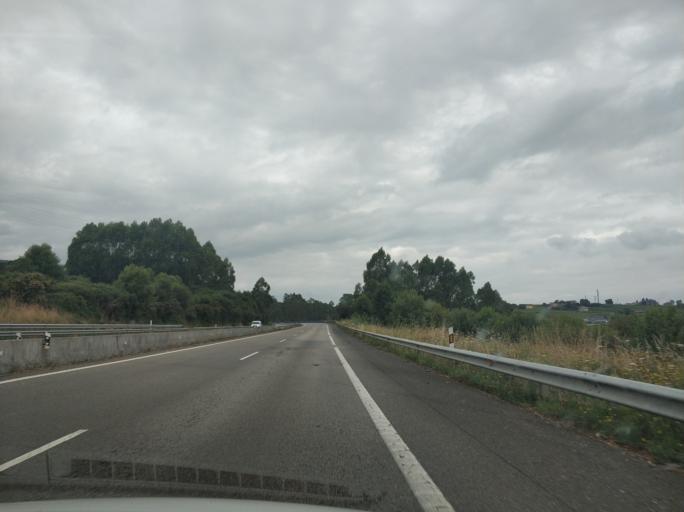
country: ES
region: Asturias
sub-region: Province of Asturias
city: Navia
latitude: 43.5307
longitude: -6.7289
